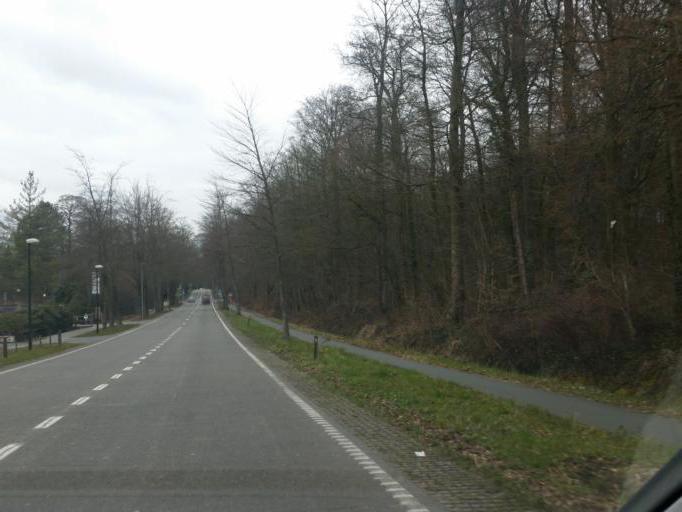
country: BE
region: Flanders
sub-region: Provincie Vlaams-Brabant
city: Sint-Genesius-Rode
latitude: 50.7843
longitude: 4.3872
